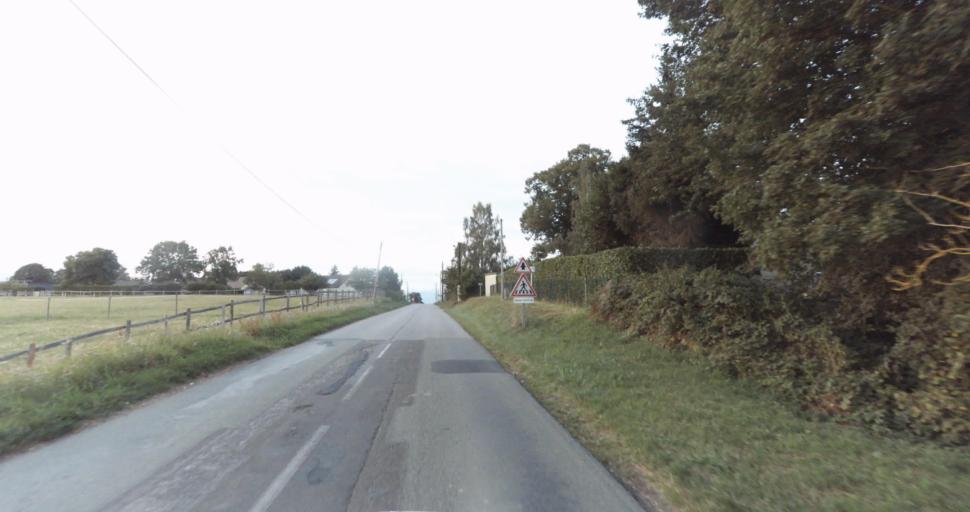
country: FR
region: Haute-Normandie
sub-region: Departement de l'Eure
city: Marcilly-sur-Eure
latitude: 48.8809
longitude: 1.2633
